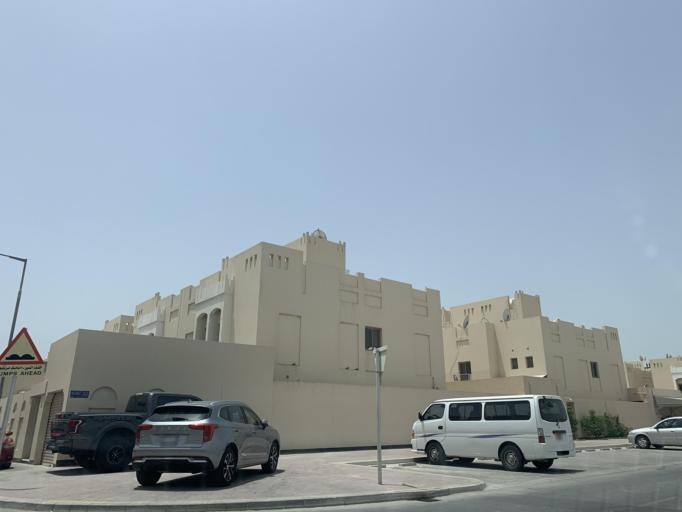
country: BH
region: Northern
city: Sitrah
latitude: 26.1469
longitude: 50.5894
